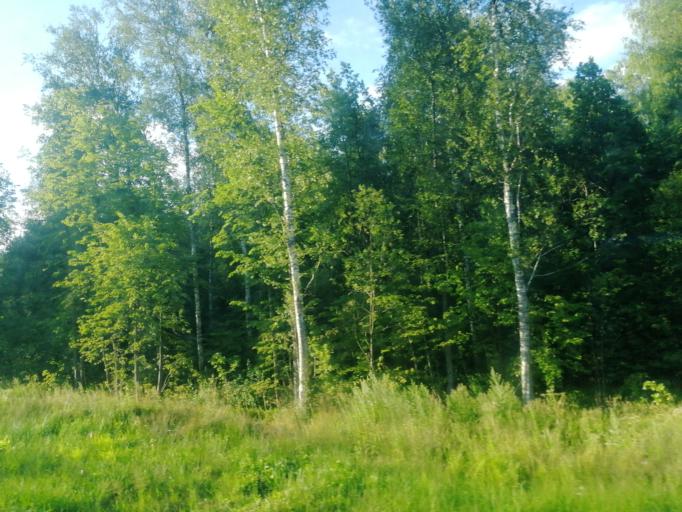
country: RU
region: Kaluga
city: Kaluga
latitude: 54.4472
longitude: 36.3108
